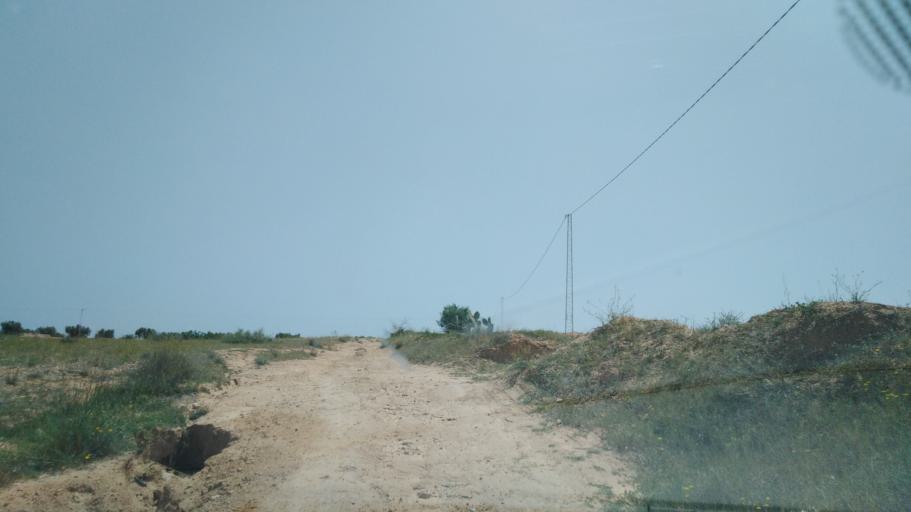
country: TN
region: Safaqis
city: Sfax
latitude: 34.7210
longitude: 10.5691
